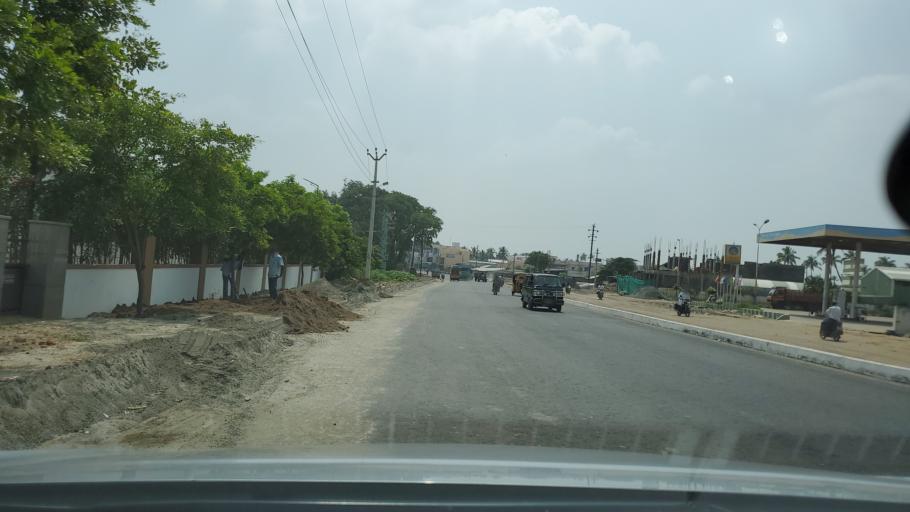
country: IN
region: Tamil Nadu
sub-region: Tiruppur
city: Kangayam
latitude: 10.9458
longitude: 77.4357
